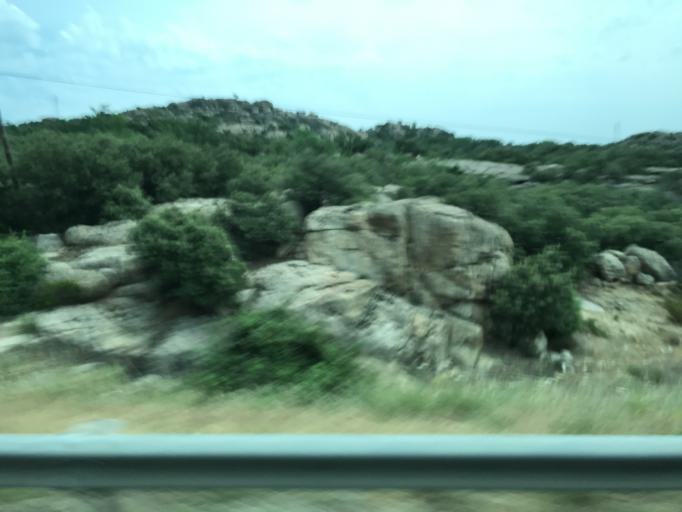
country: ES
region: Madrid
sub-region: Provincia de Madrid
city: La Cabrera
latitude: 40.8652
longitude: -3.6062
